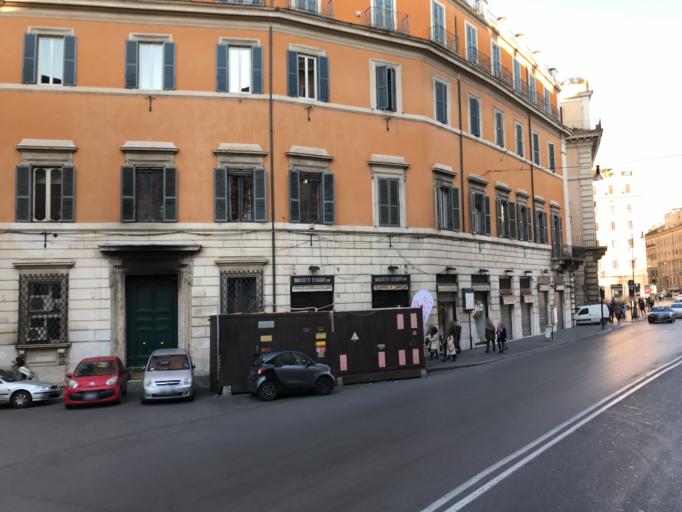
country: VA
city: Vatican City
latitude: 41.8963
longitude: 12.4757
